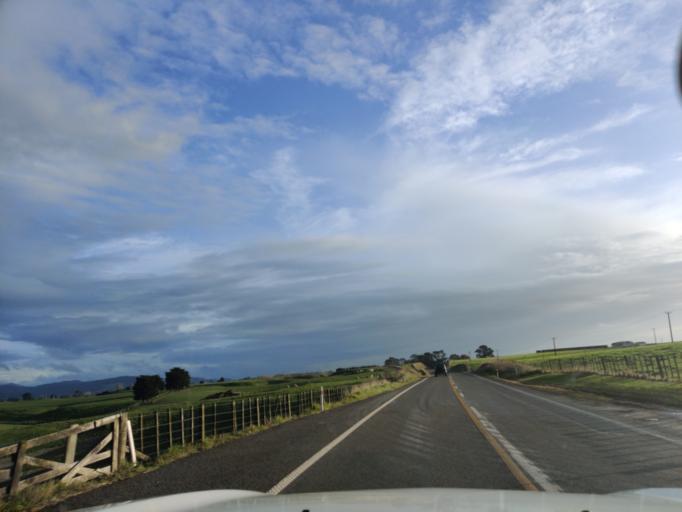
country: NZ
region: Manawatu-Wanganui
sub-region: Horowhenua District
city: Foxton
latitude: -40.5099
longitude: 175.4713
